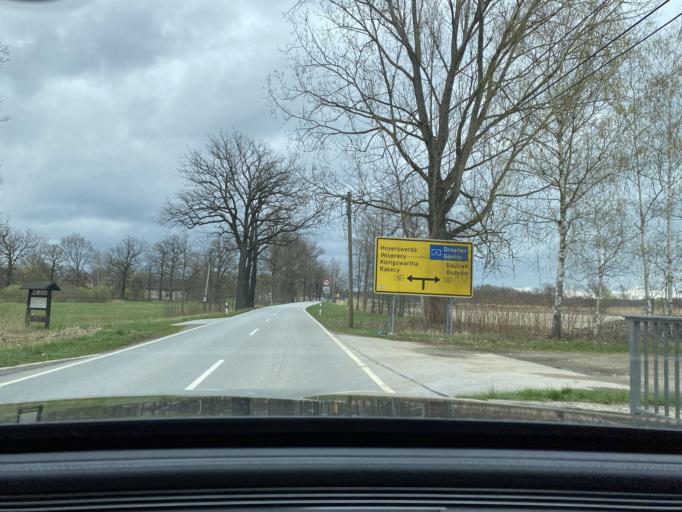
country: DE
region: Saxony
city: Neschwitz
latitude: 51.2668
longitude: 14.3407
